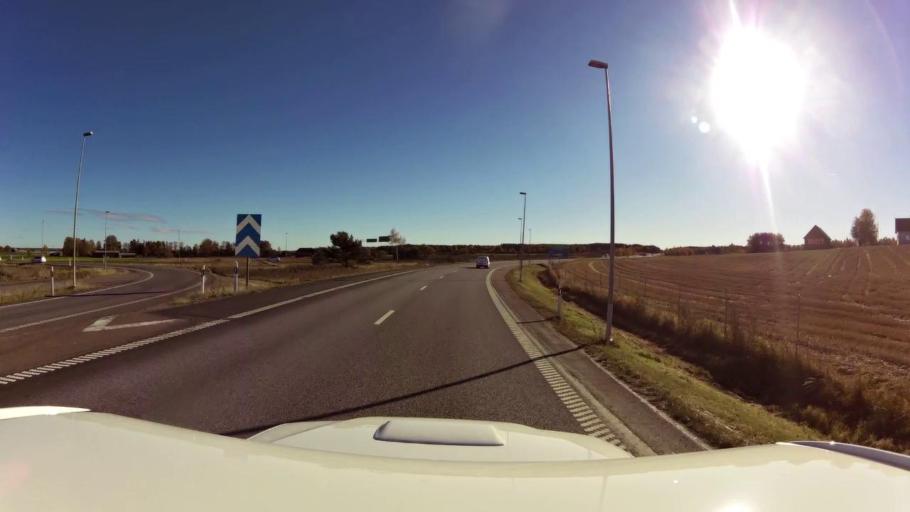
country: SE
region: OEstergoetland
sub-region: Linkopings Kommun
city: Malmslatt
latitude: 58.4321
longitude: 15.5316
